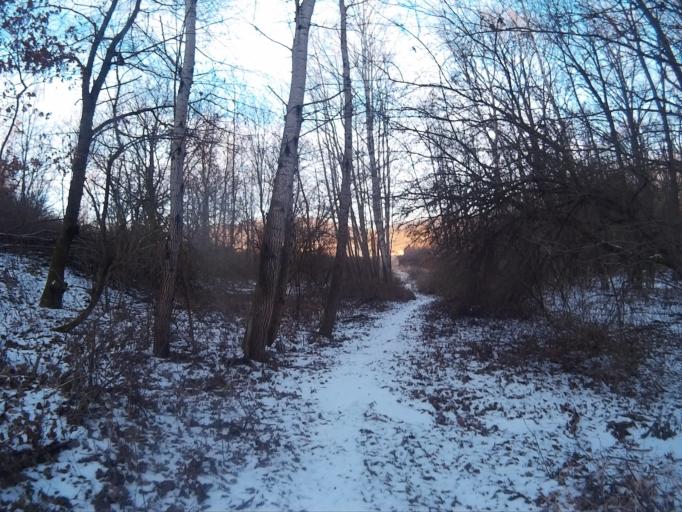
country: HU
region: Borsod-Abauj-Zemplen
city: Putnok
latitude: 48.4684
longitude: 20.4774
